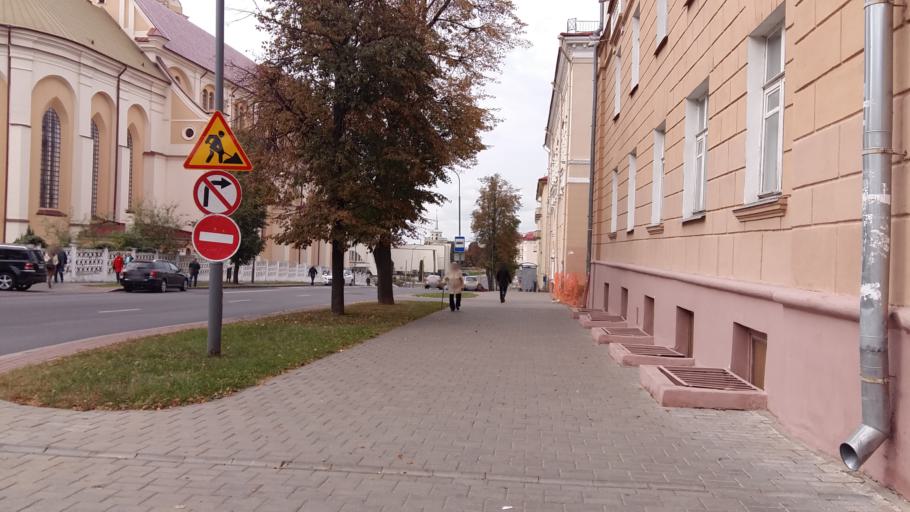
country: BY
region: Grodnenskaya
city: Hrodna
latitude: 53.6751
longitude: 23.8321
